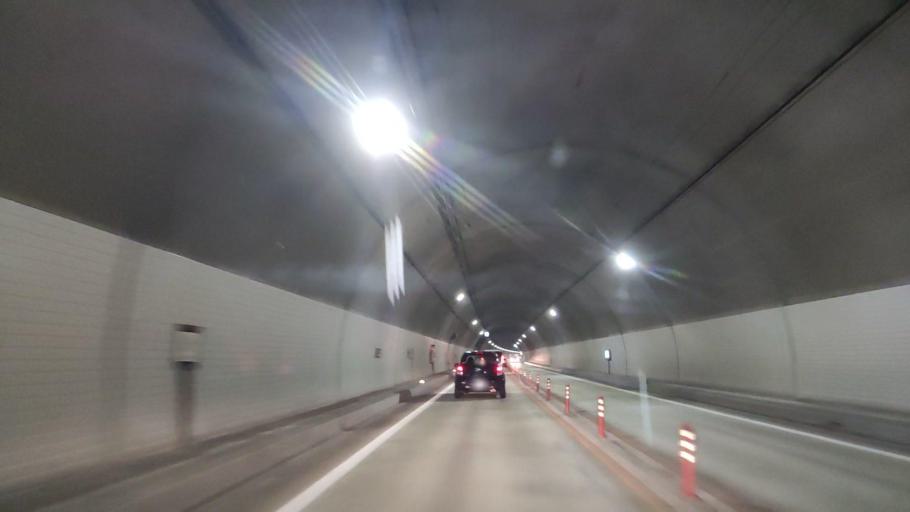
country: JP
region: Akita
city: Odate
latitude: 40.2252
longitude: 140.4689
